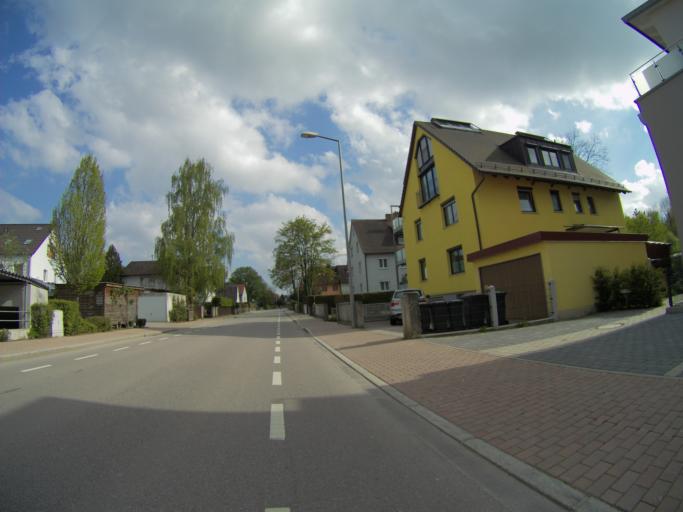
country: DE
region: Bavaria
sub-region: Upper Bavaria
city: Freising
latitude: 48.3951
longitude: 11.7524
